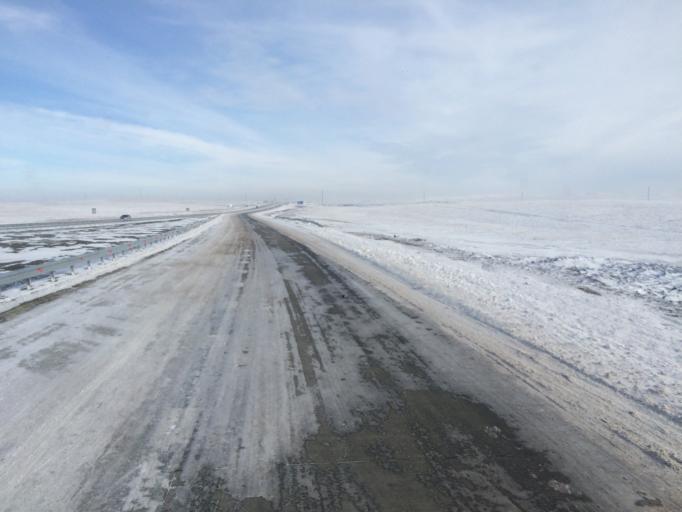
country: KZ
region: Zhambyl
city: Georgiyevka
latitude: 43.3500
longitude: 74.5467
